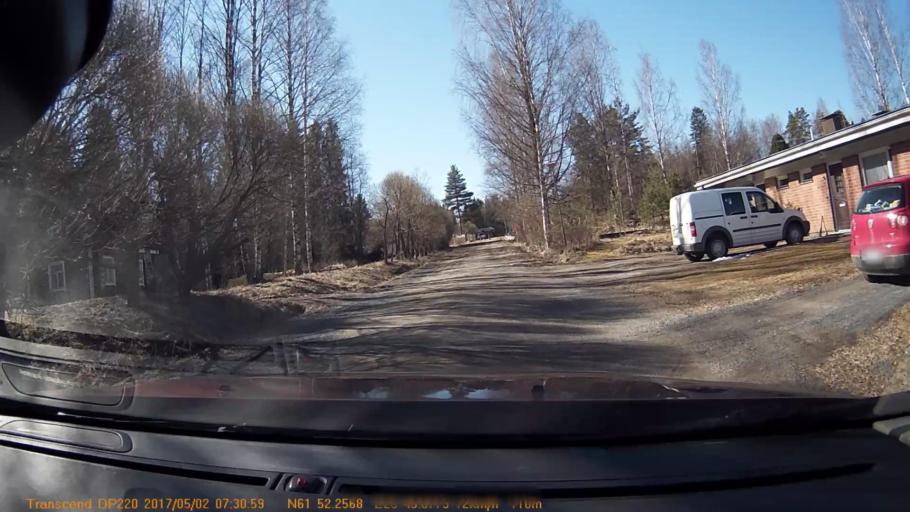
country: FI
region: Pirkanmaa
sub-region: Tampere
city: Kuru
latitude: 61.8710
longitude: 23.7280
